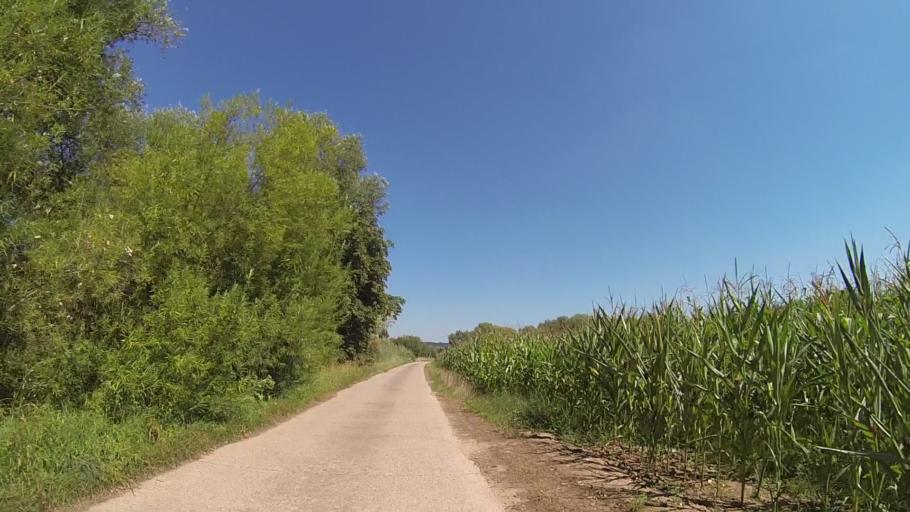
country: LU
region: Grevenmacher
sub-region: Canton de Remich
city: Remich
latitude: 49.5301
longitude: 6.3599
